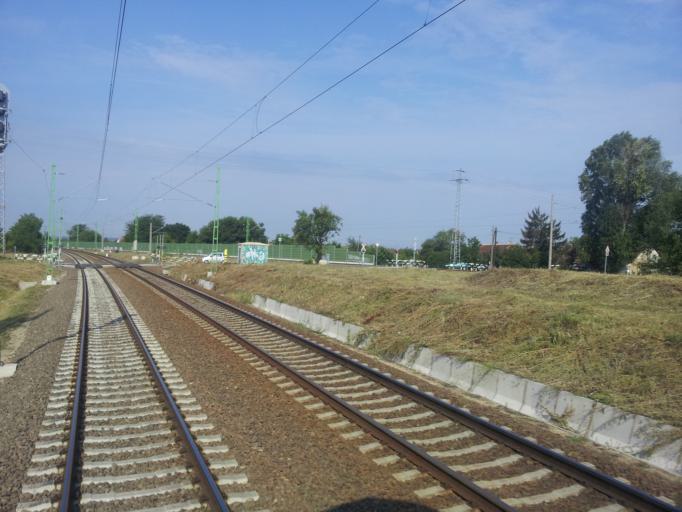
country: HU
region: Pest
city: Erd
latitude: 47.3754
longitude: 18.8963
